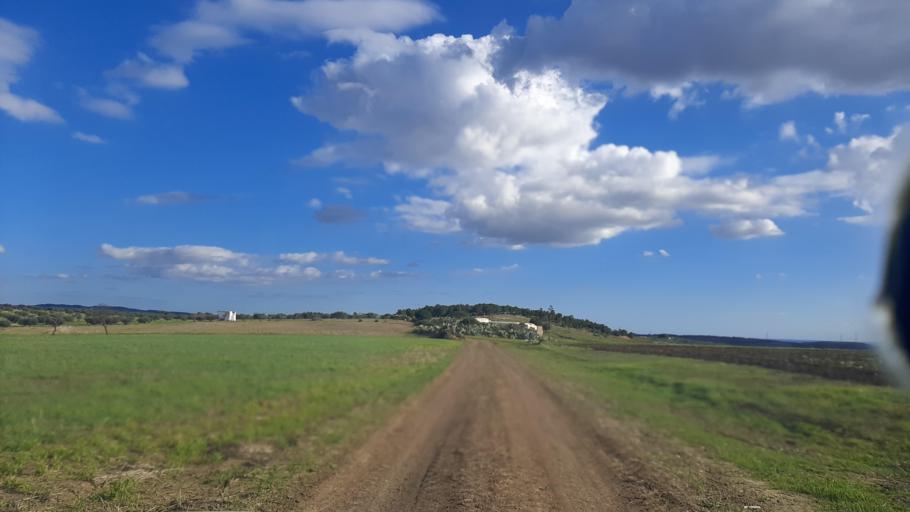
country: TN
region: Nabul
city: Bu `Urqub
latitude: 36.4616
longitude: 10.4868
